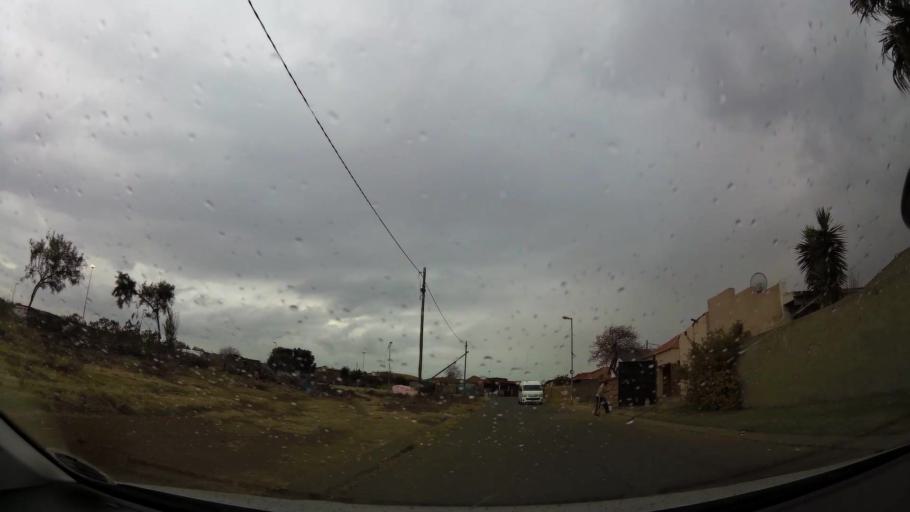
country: ZA
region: Gauteng
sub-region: City of Johannesburg Metropolitan Municipality
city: Soweto
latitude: -26.2582
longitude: 27.8727
